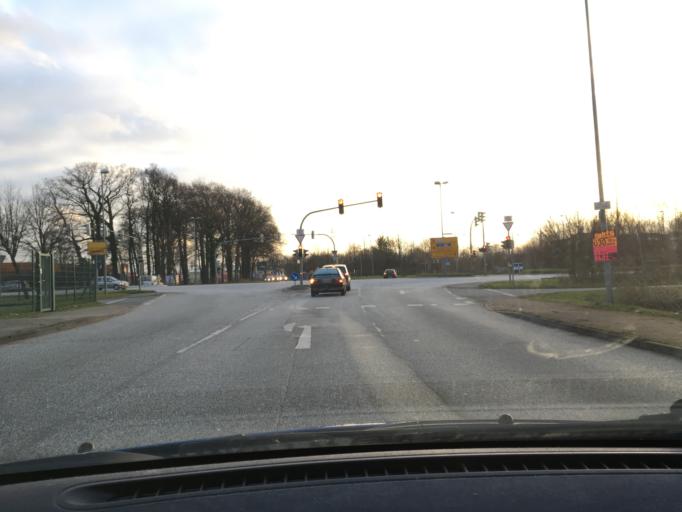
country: DE
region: Schleswig-Holstein
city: Kolln-Reisiek
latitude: 53.7451
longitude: 9.7065
